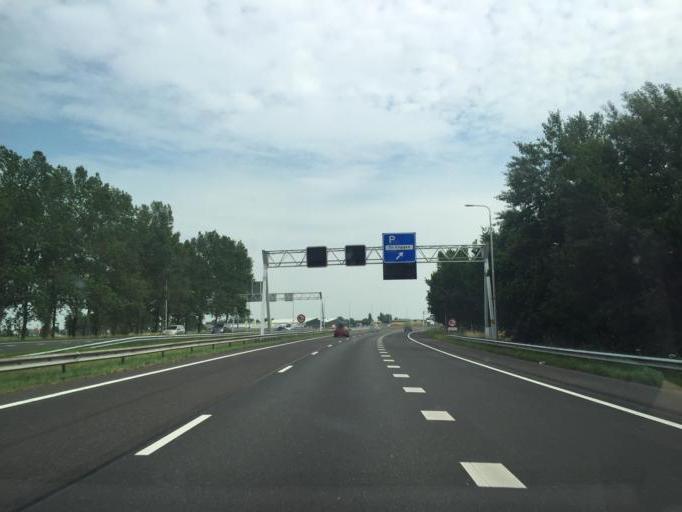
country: NL
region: North Holland
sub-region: Gemeente Hoorn
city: Hoorn
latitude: 52.6353
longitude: 5.0091
